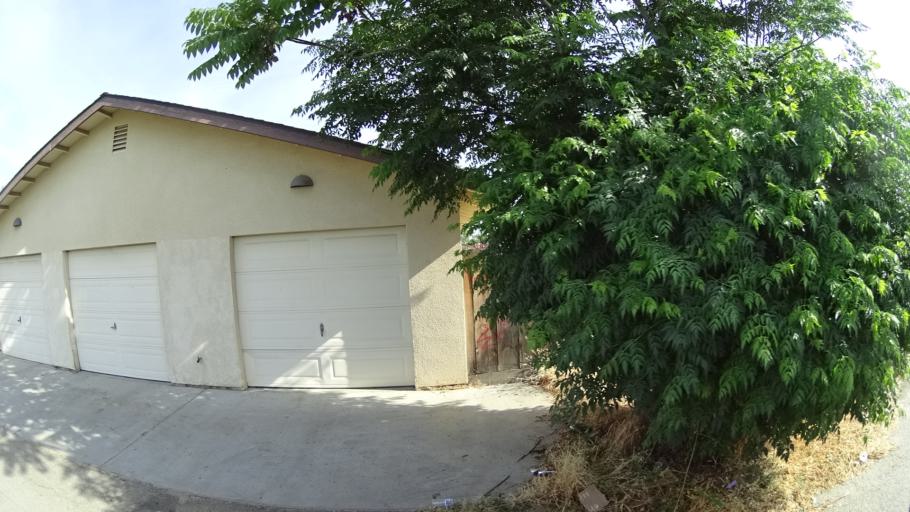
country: US
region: California
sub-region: Kings County
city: Hanford
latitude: 36.3208
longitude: -119.6452
